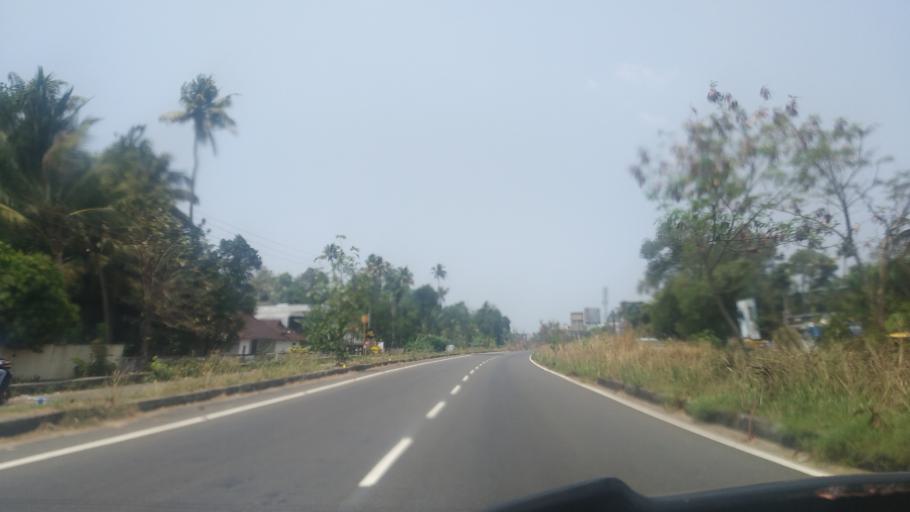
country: IN
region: Kerala
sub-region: Thrissur District
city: Kodungallur
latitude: 10.2275
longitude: 76.1956
